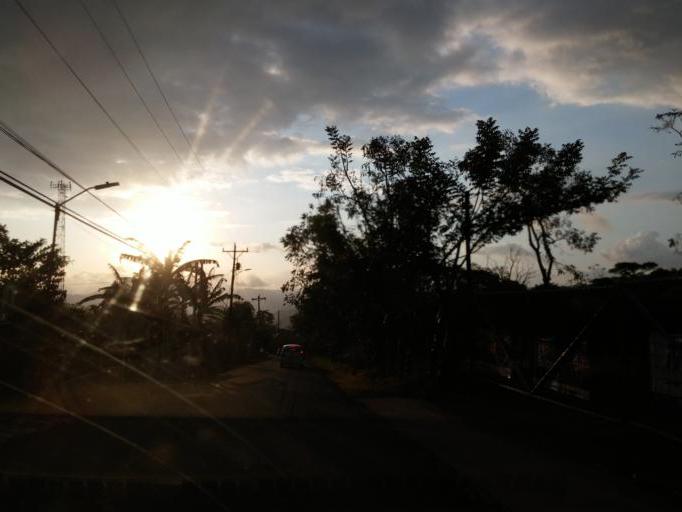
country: CR
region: San Jose
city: Palmichal
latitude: 9.8488
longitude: -84.2253
